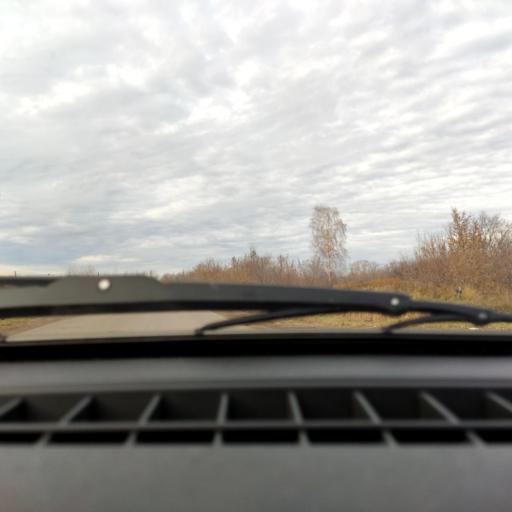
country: RU
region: Bashkortostan
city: Ufa
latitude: 54.8703
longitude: 56.1330
